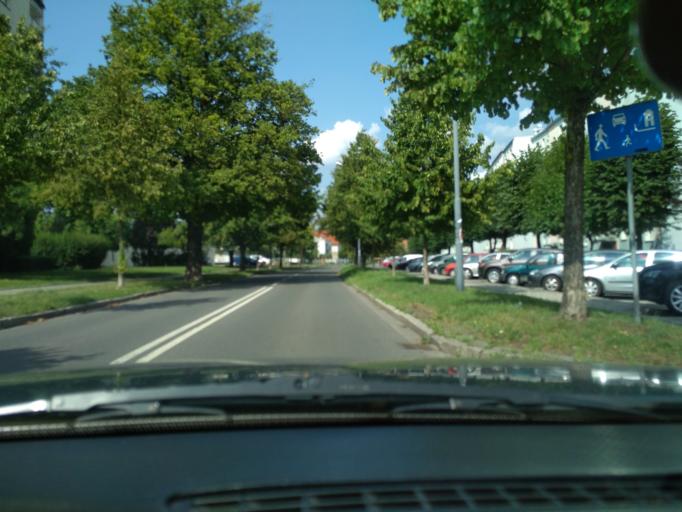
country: PL
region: Silesian Voivodeship
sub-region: Powiat raciborski
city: Raciborz
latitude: 50.0899
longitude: 18.2083
